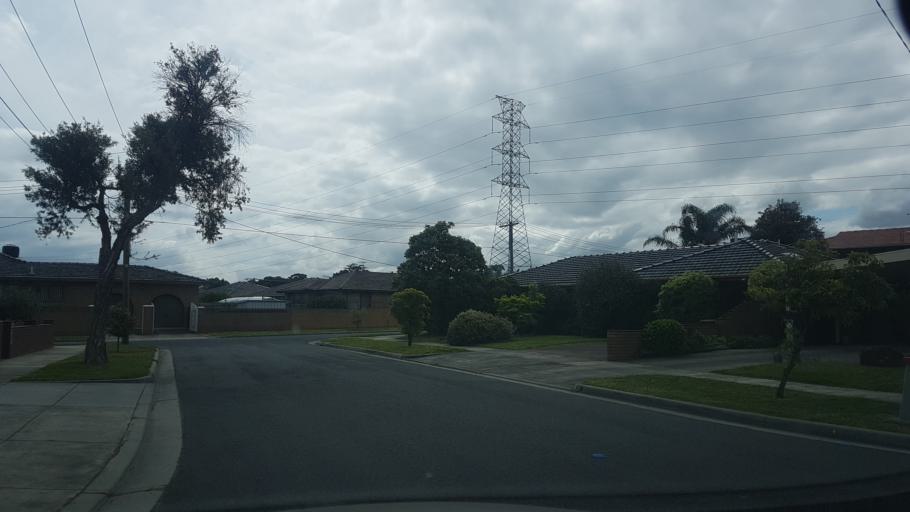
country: AU
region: Victoria
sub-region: Monash
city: Oakleigh South
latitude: -37.9370
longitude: 145.0841
